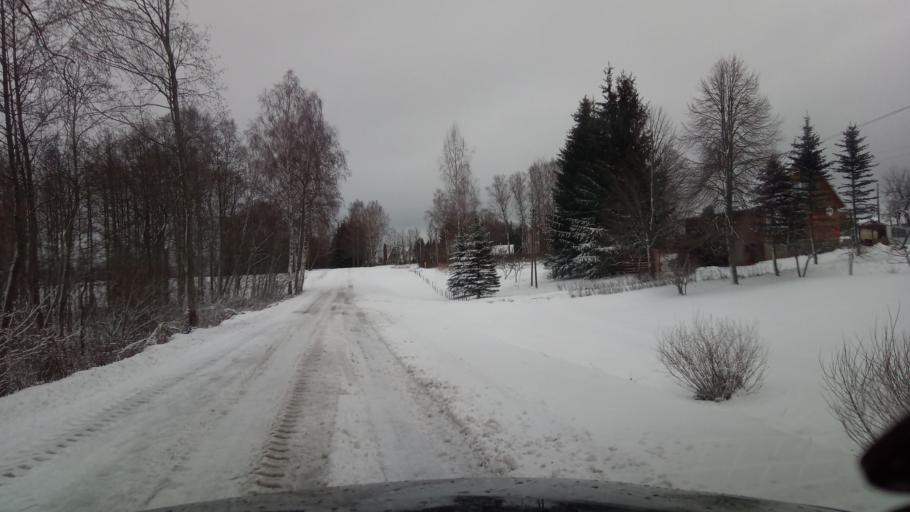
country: LT
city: Zarasai
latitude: 55.6231
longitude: 25.9549
